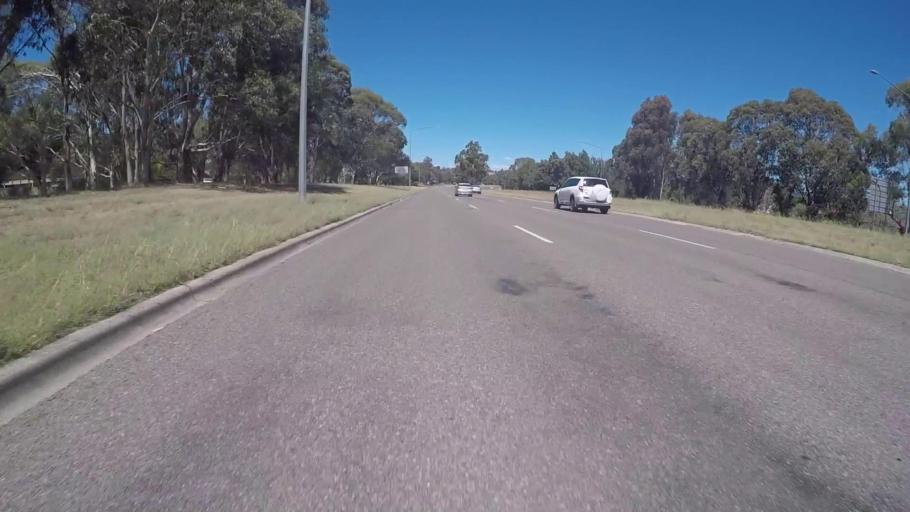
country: AU
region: Australian Capital Territory
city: Macarthur
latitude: -35.3985
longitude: 149.0733
